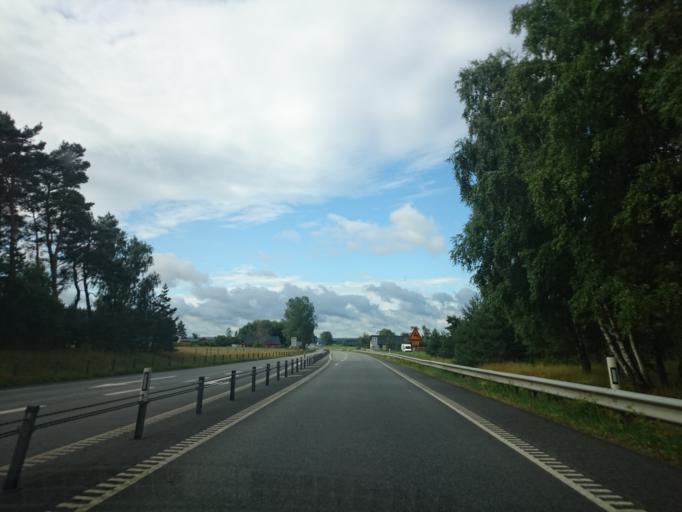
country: SE
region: Skane
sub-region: Kristianstads Kommun
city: Norra Asum
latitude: 55.9655
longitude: 14.0721
